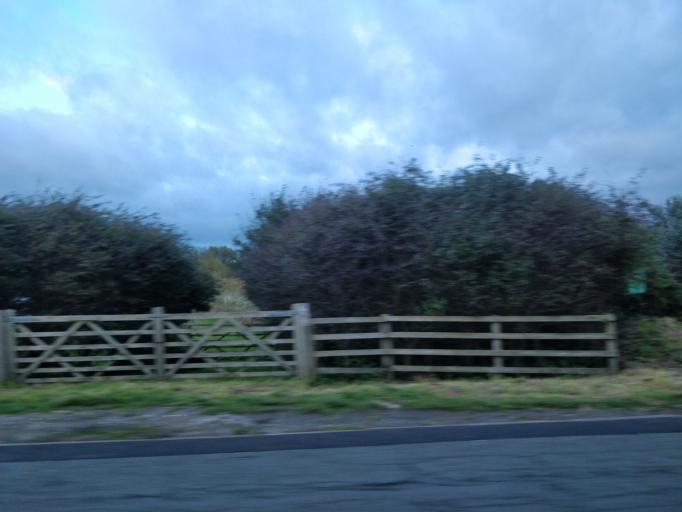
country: GB
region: England
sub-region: Sefton
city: Southport
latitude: 53.6650
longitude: -2.9902
